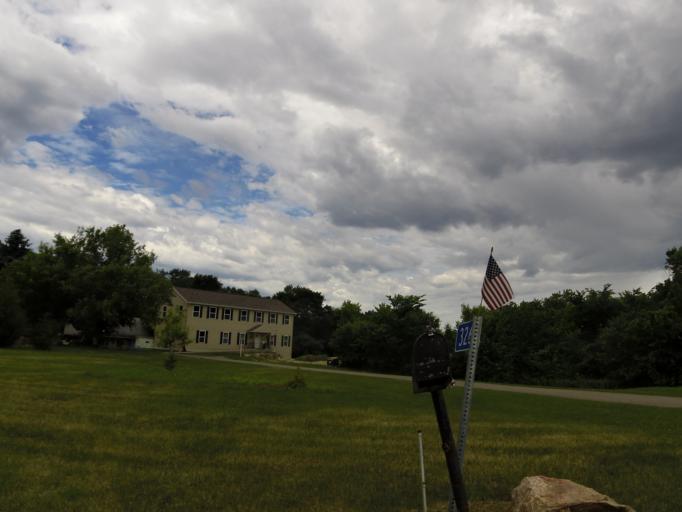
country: US
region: Minnesota
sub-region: Scott County
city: Prior Lake
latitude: 44.7567
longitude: -93.4540
